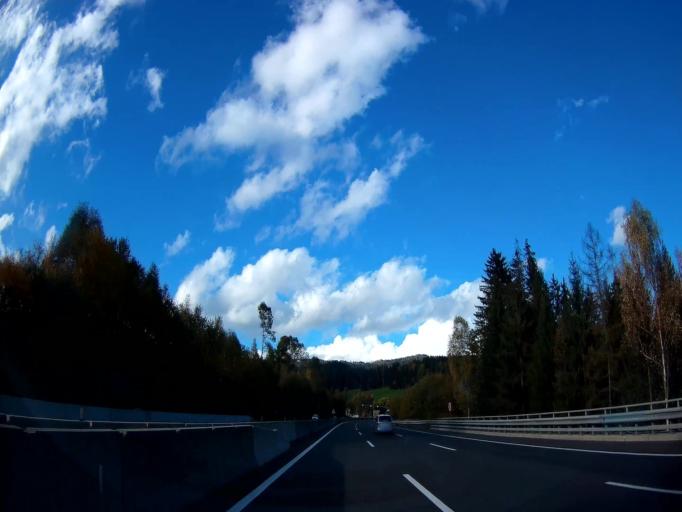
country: AT
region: Carinthia
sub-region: Politischer Bezirk Wolfsberg
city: Preitenegg
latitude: 46.9413
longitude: 14.8709
